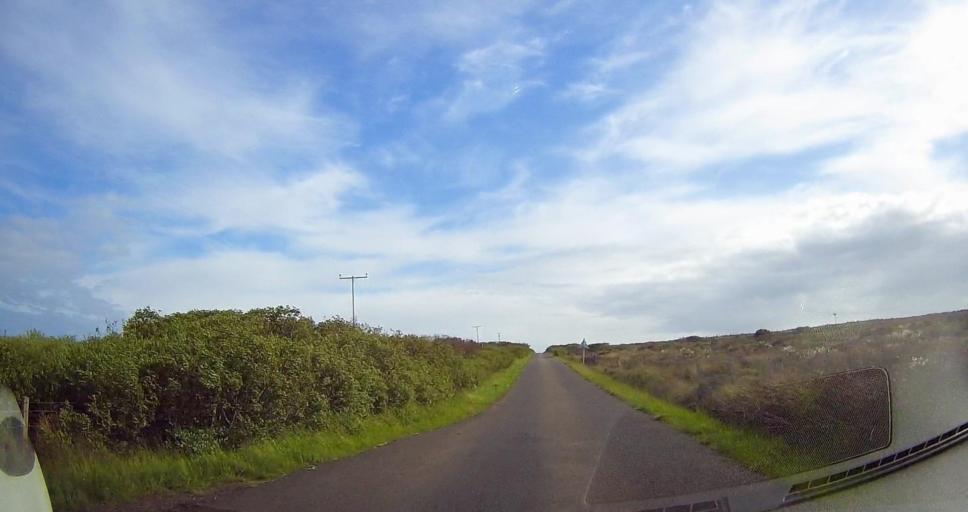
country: GB
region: Scotland
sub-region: Orkney Islands
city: Stromness
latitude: 58.8507
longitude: -3.2041
